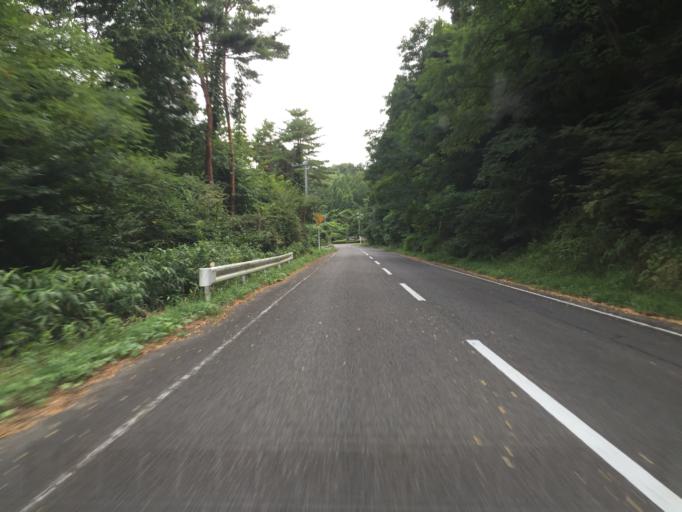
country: JP
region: Fukushima
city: Motomiya
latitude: 37.5439
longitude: 140.3214
